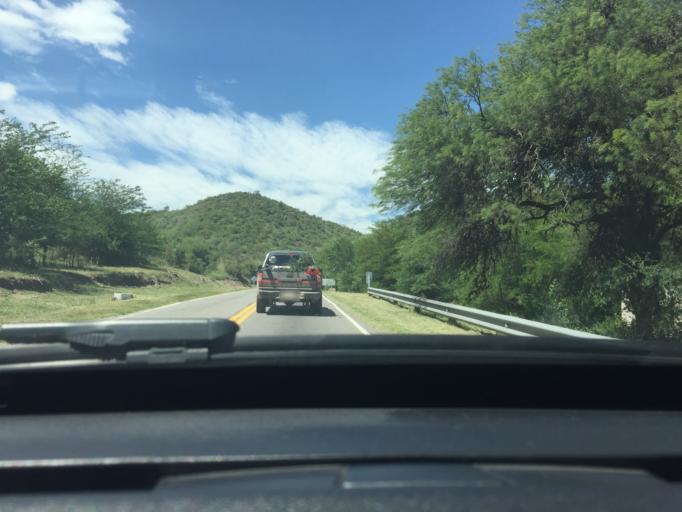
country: AR
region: Cordoba
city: Alta Gracia
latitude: -31.7434
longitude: -64.4638
